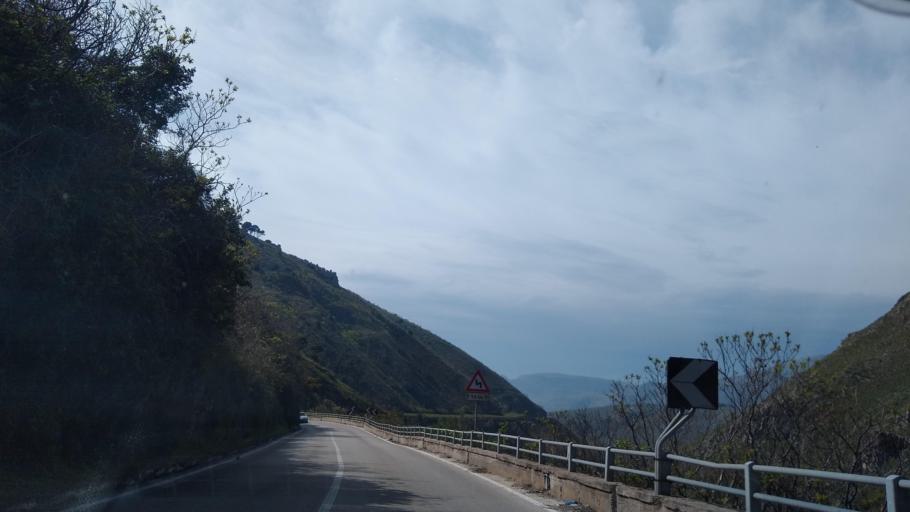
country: IT
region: Sicily
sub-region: Palermo
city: Montelepre
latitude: 38.0507
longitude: 13.1881
